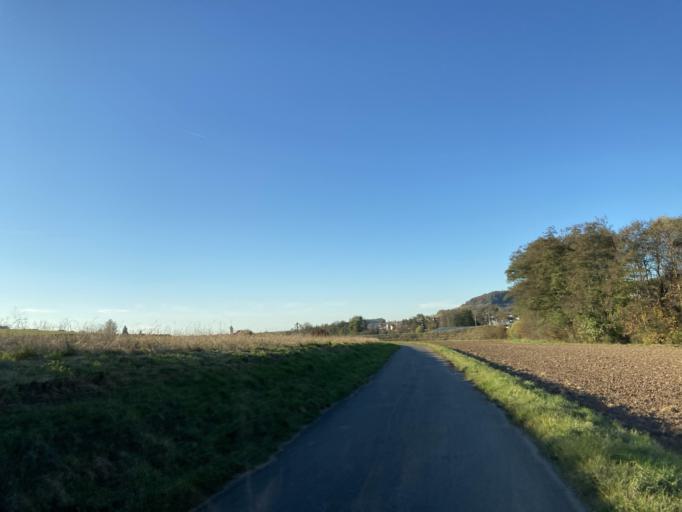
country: DE
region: Baden-Wuerttemberg
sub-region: Tuebingen Region
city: Rottenburg
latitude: 48.4314
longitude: 8.9478
